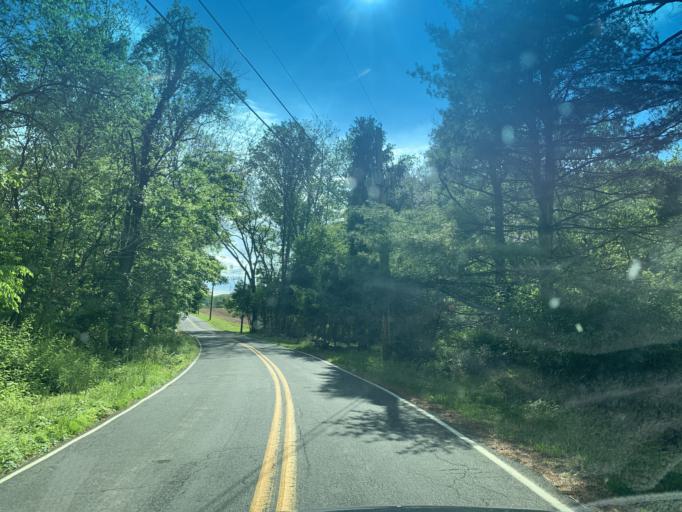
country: US
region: Maryland
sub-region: Cecil County
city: Rising Sun
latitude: 39.6909
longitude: -76.1528
